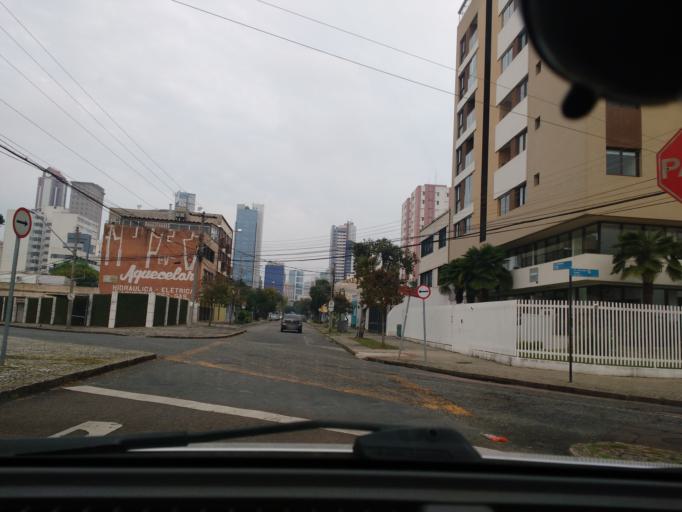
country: BR
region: Parana
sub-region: Curitiba
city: Curitiba
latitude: -25.4298
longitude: -49.2827
